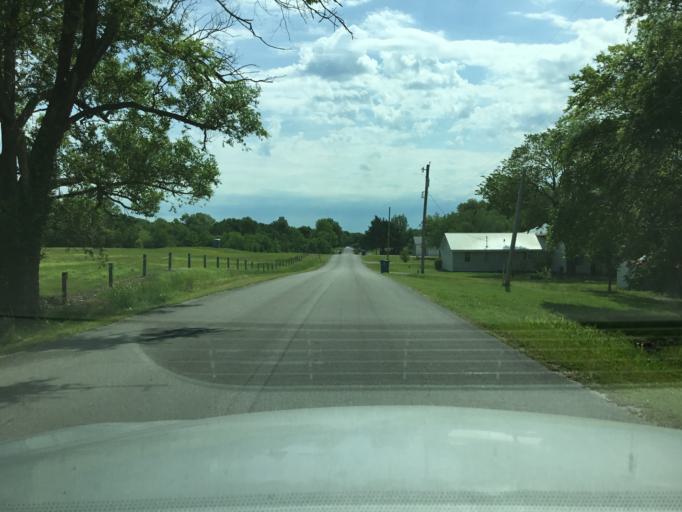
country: US
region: Kansas
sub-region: Montgomery County
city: Coffeyville
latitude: 37.0544
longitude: -95.6454
